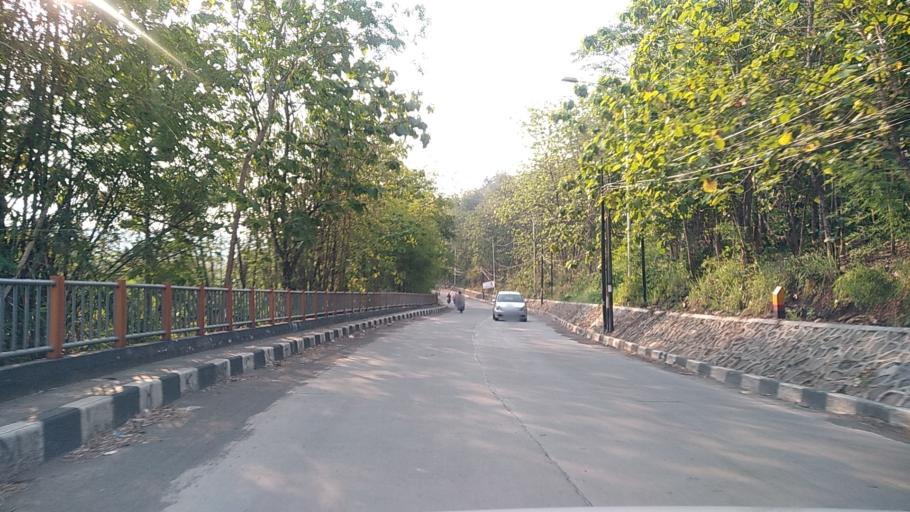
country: ID
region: Central Java
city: Mranggen
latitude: -7.0576
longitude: 110.4694
